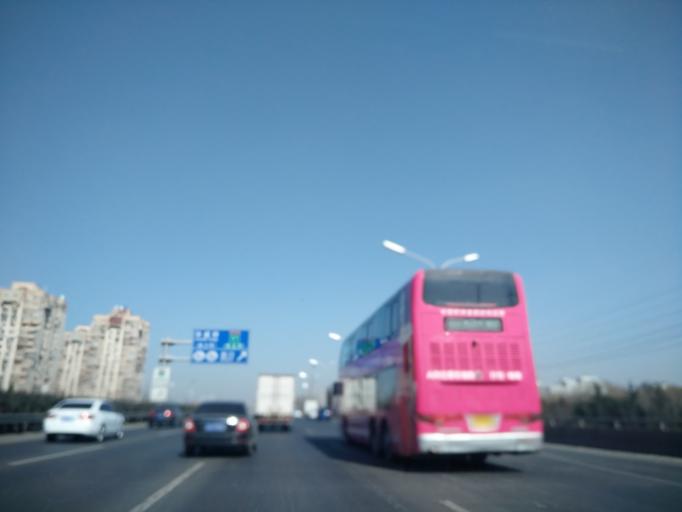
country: CN
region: Beijing
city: Longtan
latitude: 39.8647
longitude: 116.4820
